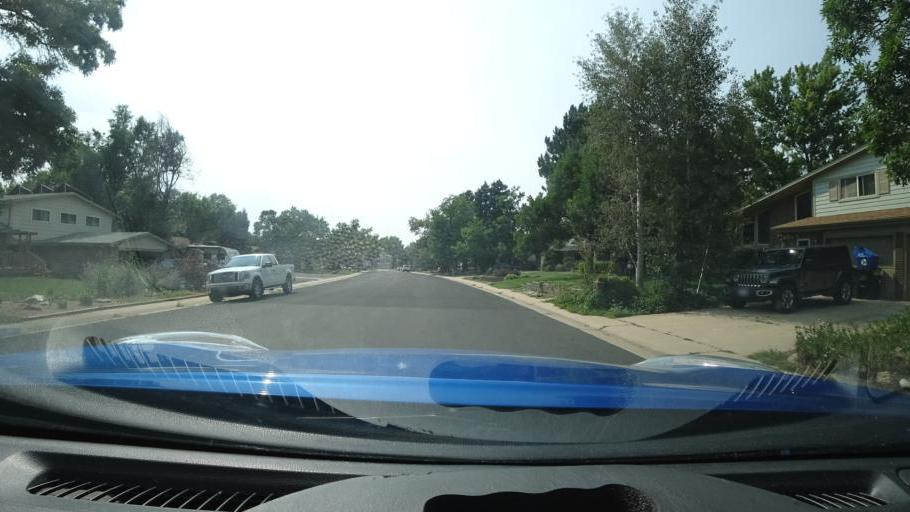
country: US
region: Colorado
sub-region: Adams County
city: Aurora
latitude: 39.6733
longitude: -104.8604
